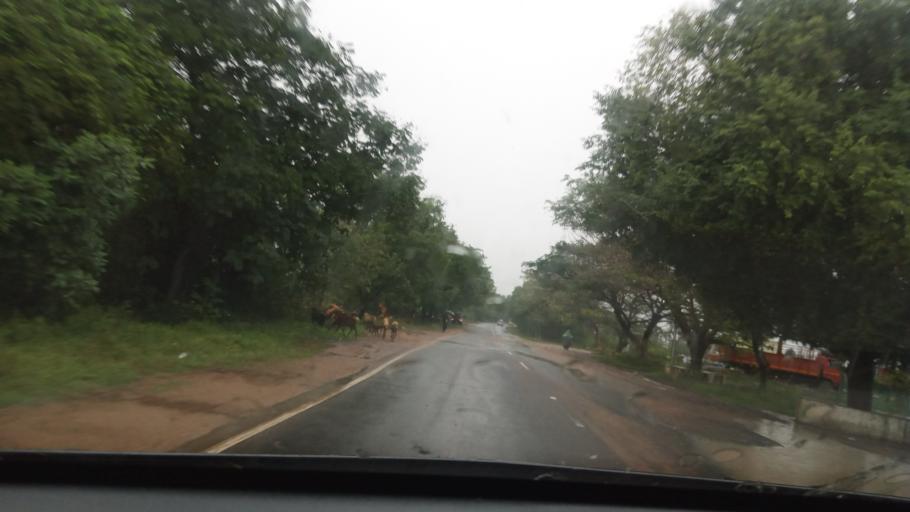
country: IN
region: Tamil Nadu
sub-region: Vellore
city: Kalavai
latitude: 12.8295
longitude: 79.4062
